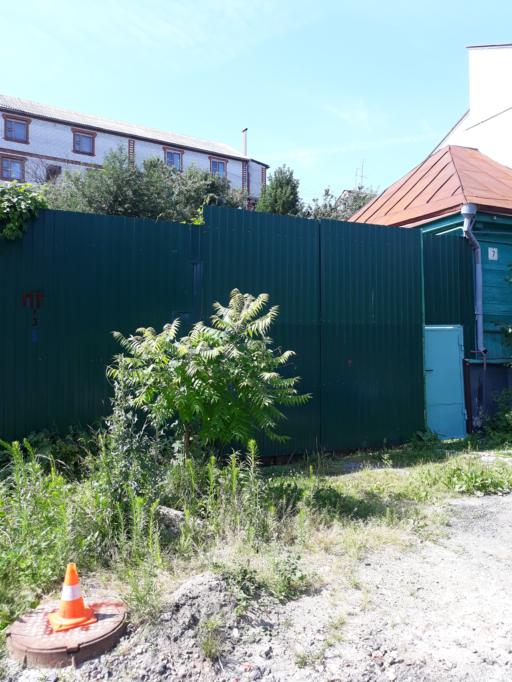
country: RU
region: Voronezj
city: Voronezh
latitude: 51.6738
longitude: 39.2240
